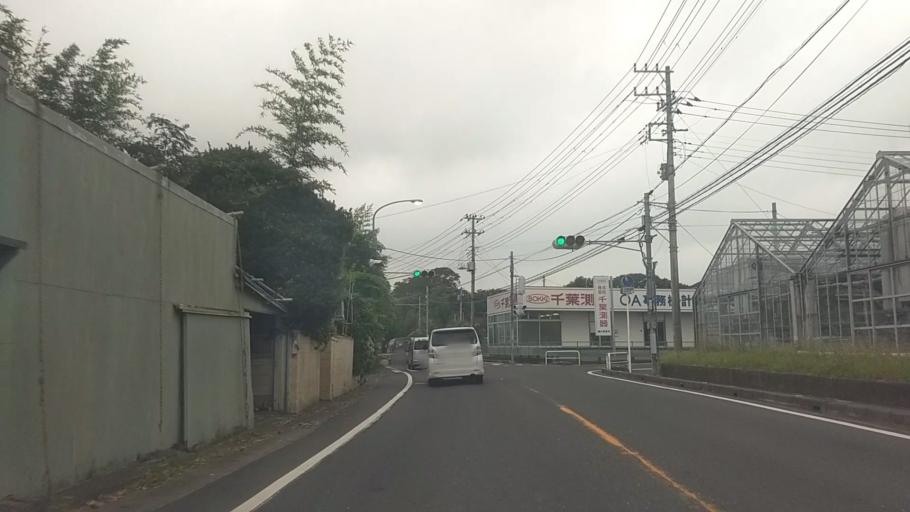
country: JP
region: Chiba
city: Kawaguchi
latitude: 35.1088
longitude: 140.0901
